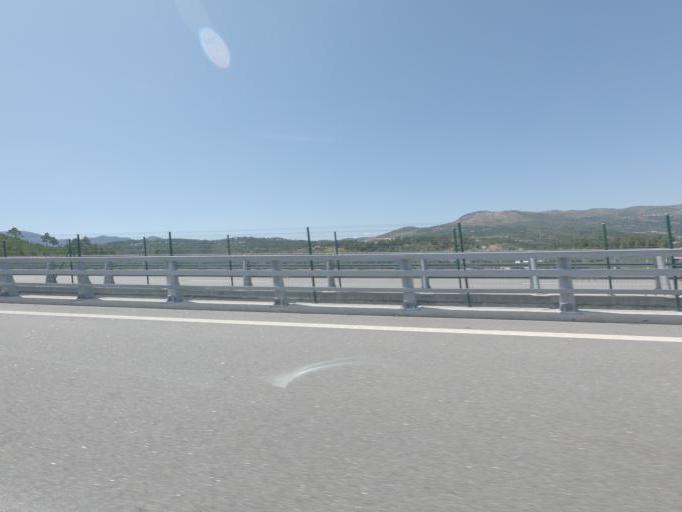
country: PT
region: Vila Real
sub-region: Vila Real
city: Vila Real
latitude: 41.2685
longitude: -7.7854
